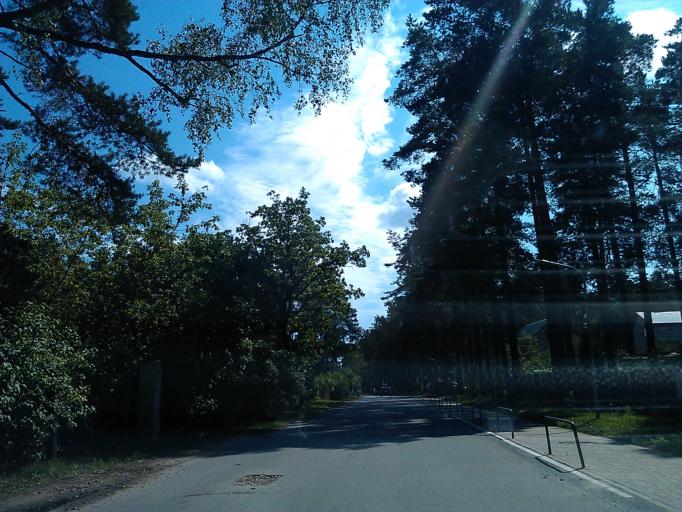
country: LV
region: Riga
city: Bergi
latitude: 57.0094
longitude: 24.3270
